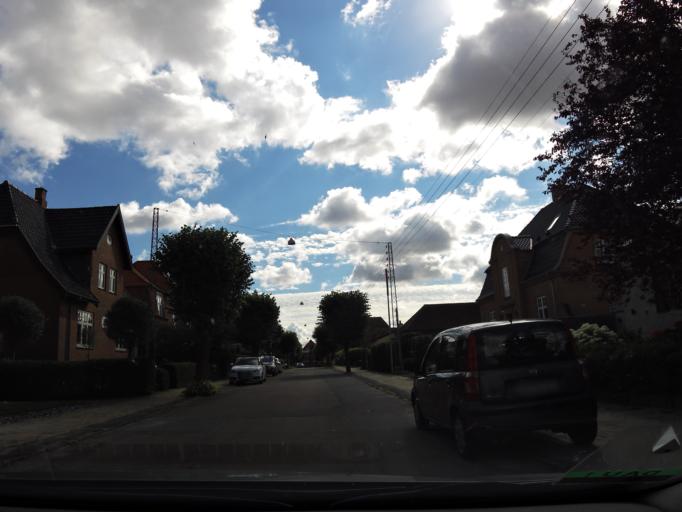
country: DK
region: South Denmark
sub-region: Odense Kommune
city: Odense
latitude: 55.3848
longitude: 10.3926
